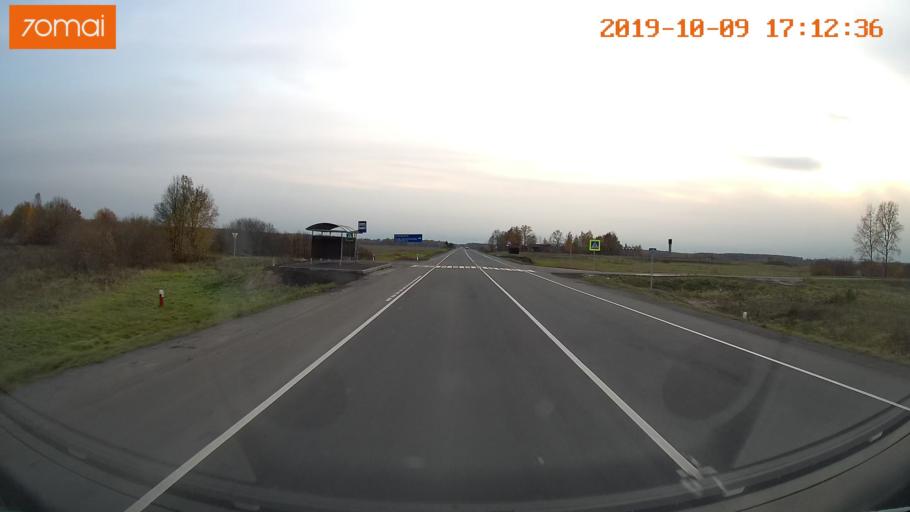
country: RU
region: Ivanovo
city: Privolzhsk
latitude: 57.3265
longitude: 41.2392
